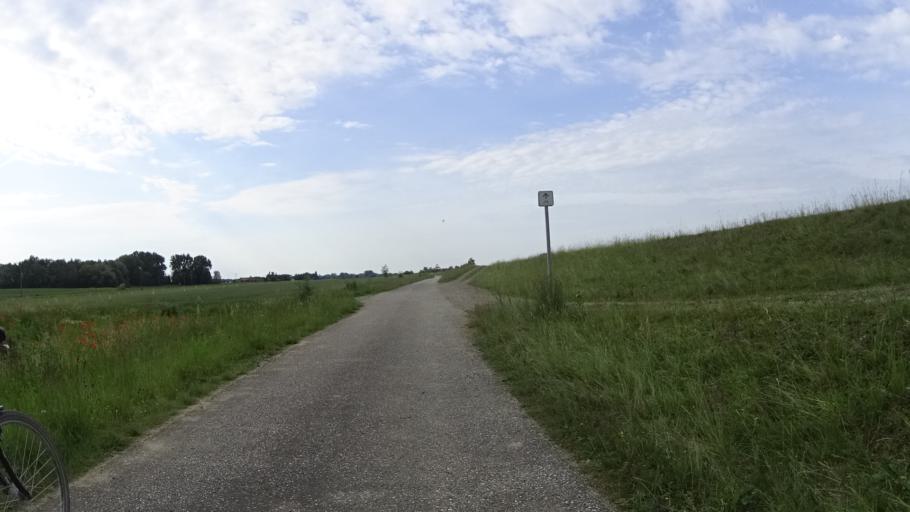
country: DE
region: Bavaria
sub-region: Lower Bavaria
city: Irlbach
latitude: 48.8628
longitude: 12.7629
